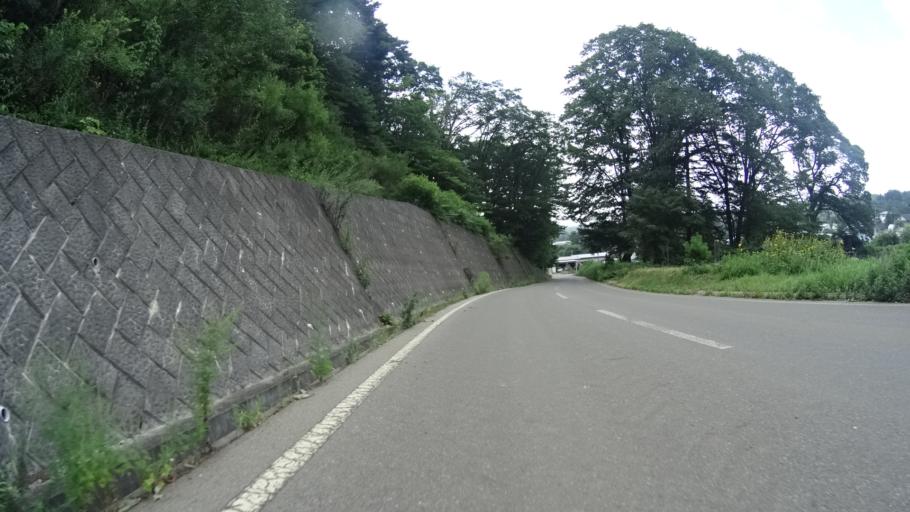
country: JP
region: Yamanashi
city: Nirasaki
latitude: 35.9149
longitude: 138.4526
